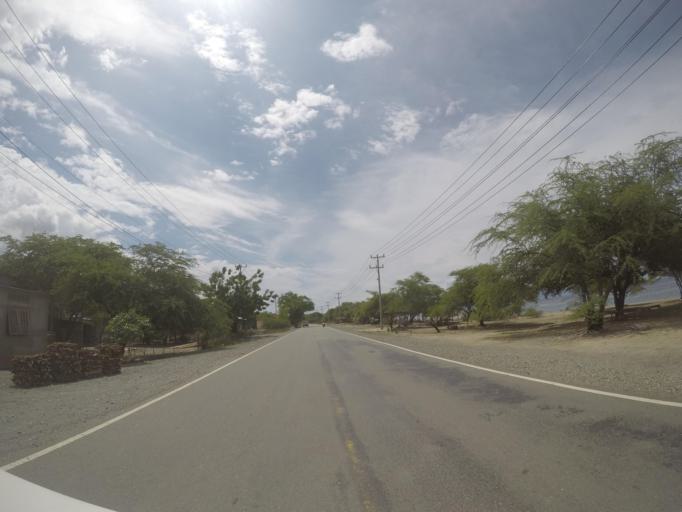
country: TL
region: Liquica
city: Liquica
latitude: -8.5650
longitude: 125.3964
